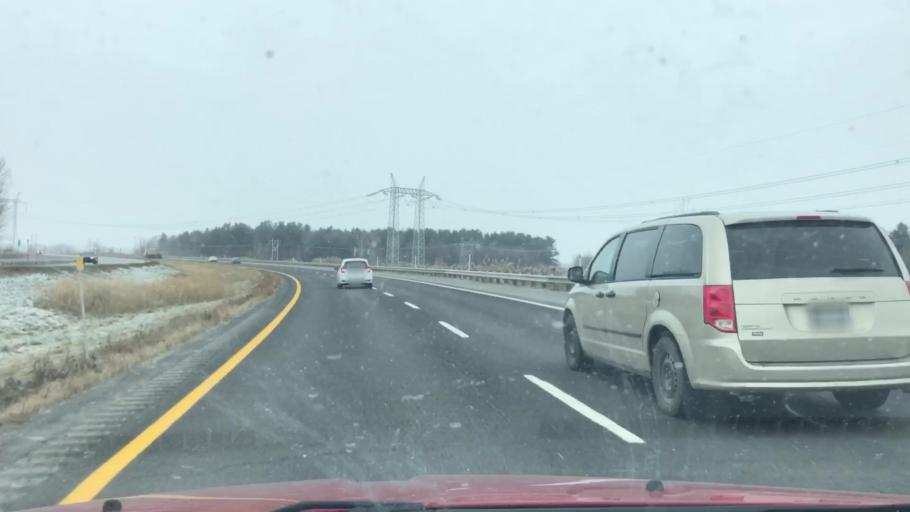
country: CA
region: Quebec
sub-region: Monteregie
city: Marieville
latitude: 45.4157
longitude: -73.1123
